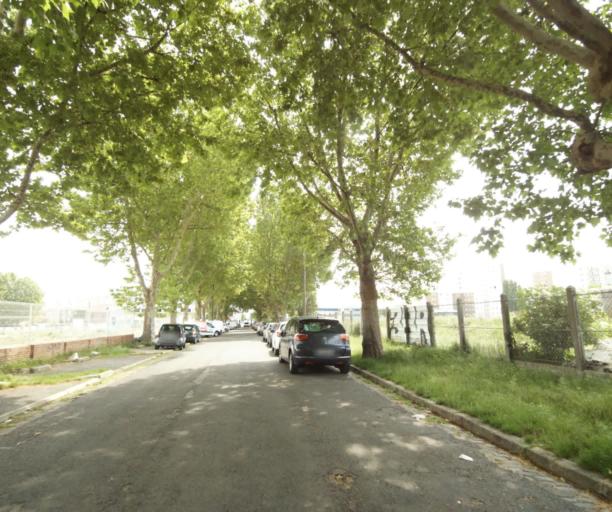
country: FR
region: Ile-de-France
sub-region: Departement des Hauts-de-Seine
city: Colombes
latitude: 48.9330
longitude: 2.2532
